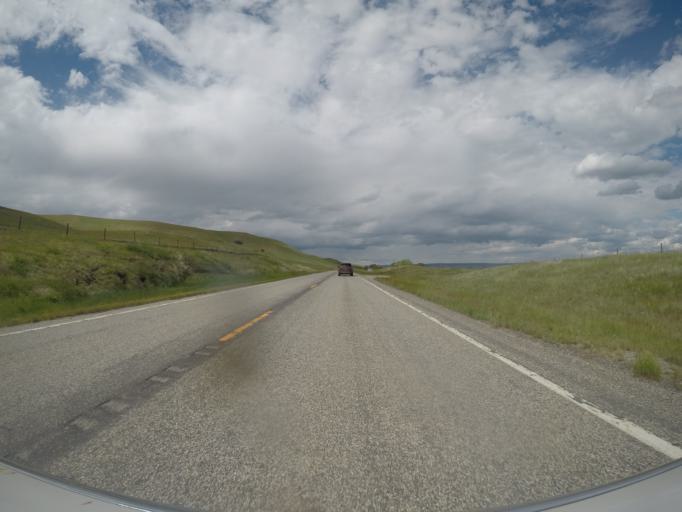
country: US
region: Montana
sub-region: Sweet Grass County
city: Big Timber
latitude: 45.8011
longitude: -109.9684
